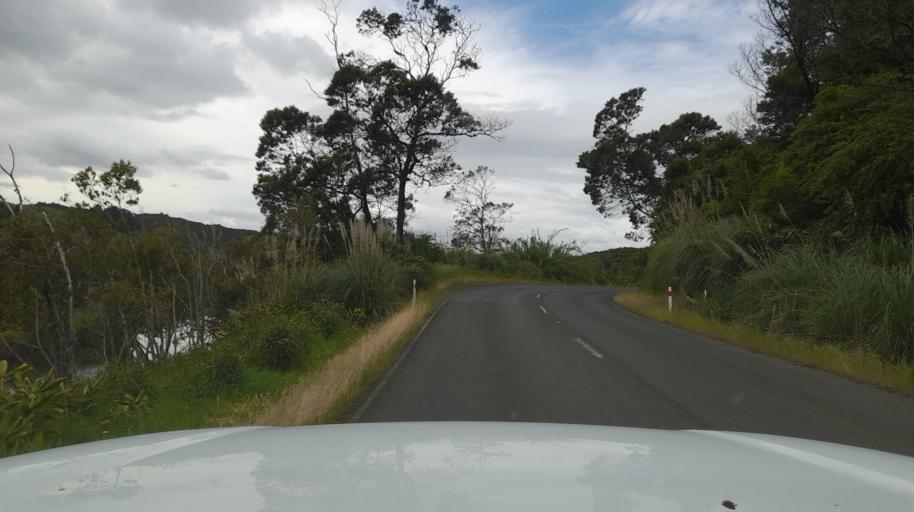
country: NZ
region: Northland
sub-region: Far North District
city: Kaitaia
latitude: -35.3929
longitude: 173.3801
